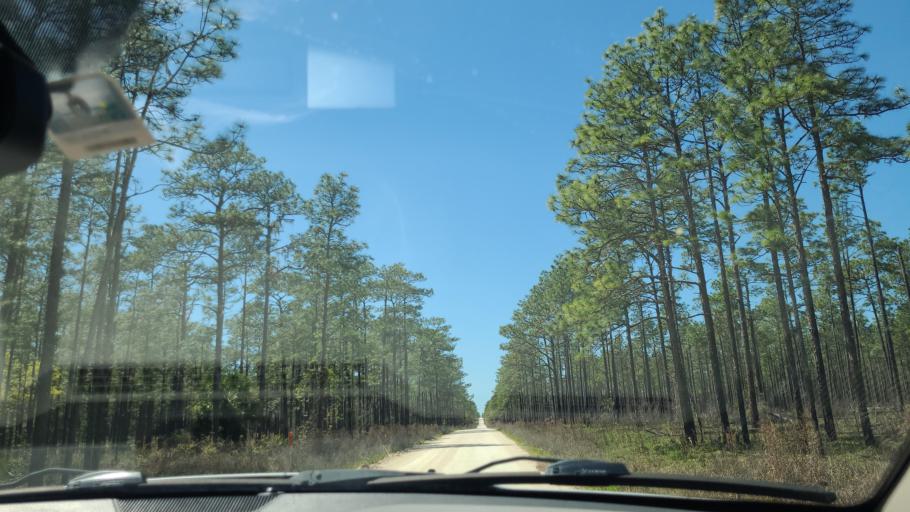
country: US
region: Florida
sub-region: Putnam County
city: Interlachen
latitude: 29.4289
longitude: -81.7935
